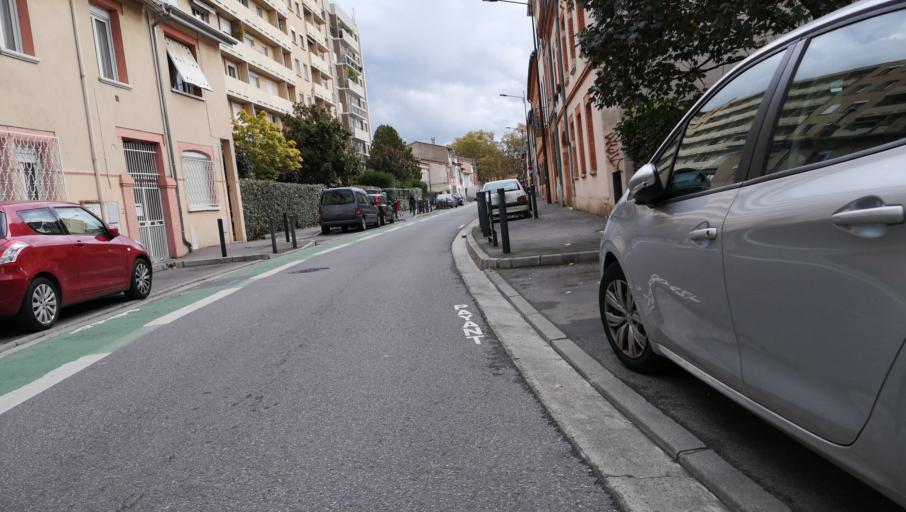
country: FR
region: Midi-Pyrenees
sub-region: Departement de la Haute-Garonne
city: Toulouse
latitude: 43.6002
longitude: 1.4260
